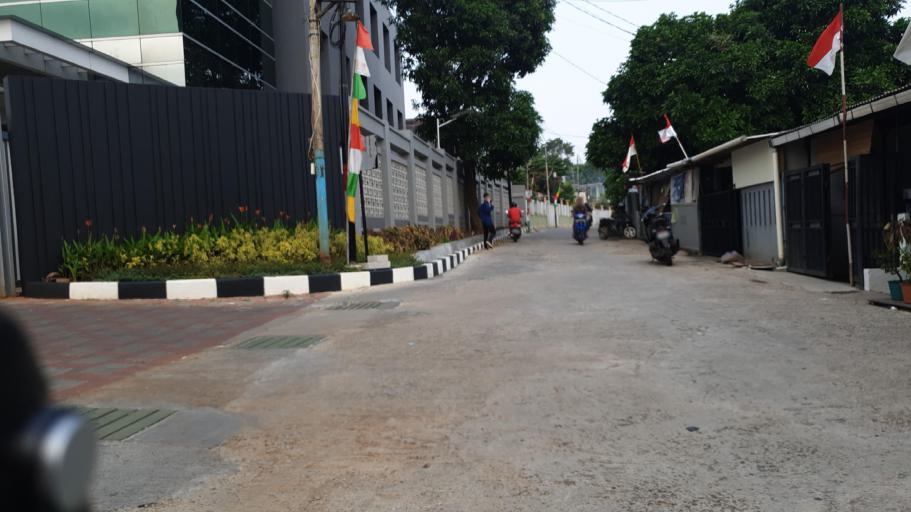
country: ID
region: West Java
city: Depok
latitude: -6.3703
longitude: 106.8400
